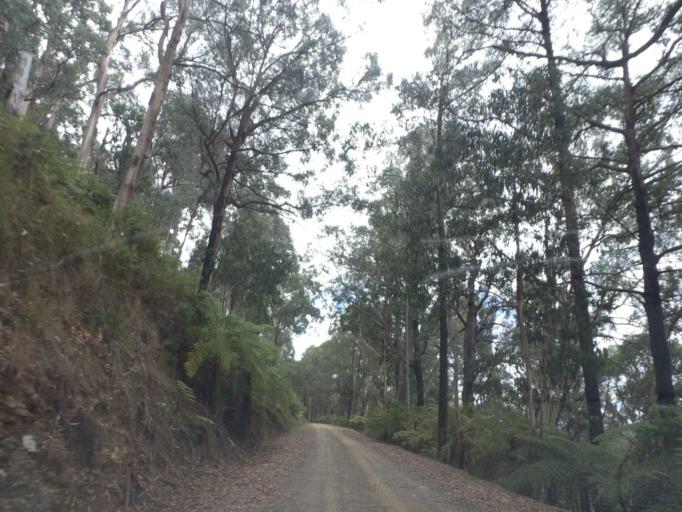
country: AU
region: Victoria
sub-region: Murrindindi
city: Alexandra
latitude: -37.4376
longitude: 145.9678
